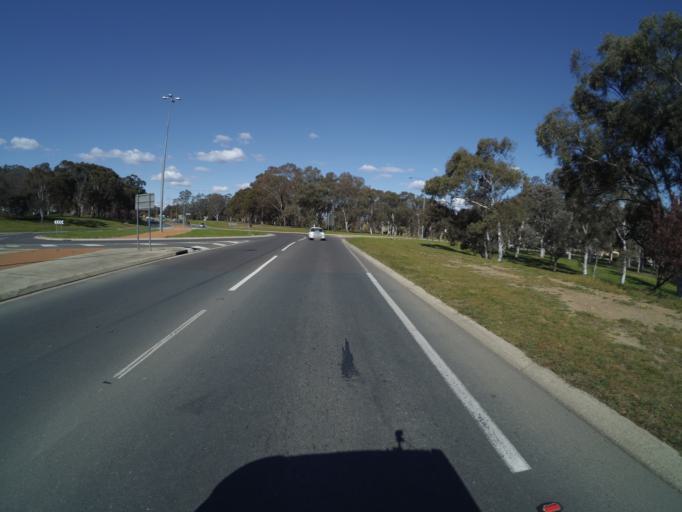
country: AU
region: Australian Capital Territory
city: Forrest
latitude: -35.3026
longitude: 149.1512
